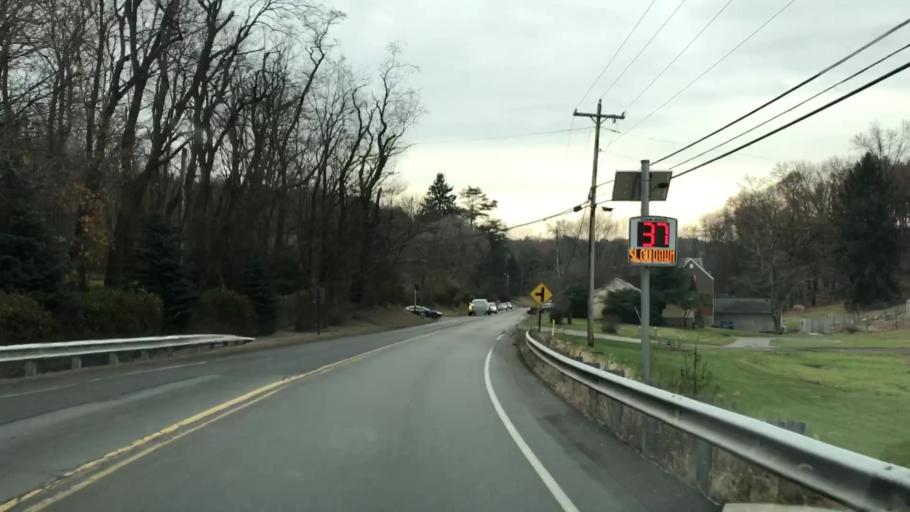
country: US
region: Pennsylvania
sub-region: Allegheny County
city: Franklin Park
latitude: 40.6009
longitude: -80.0784
